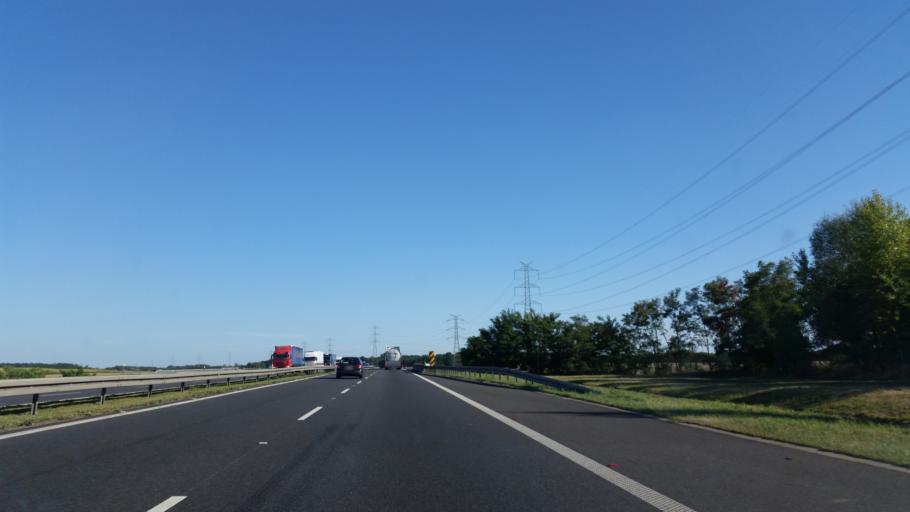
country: PL
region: Opole Voivodeship
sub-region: Powiat brzeski
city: Skarbimierz Osiedle
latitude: 50.7986
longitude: 17.3244
